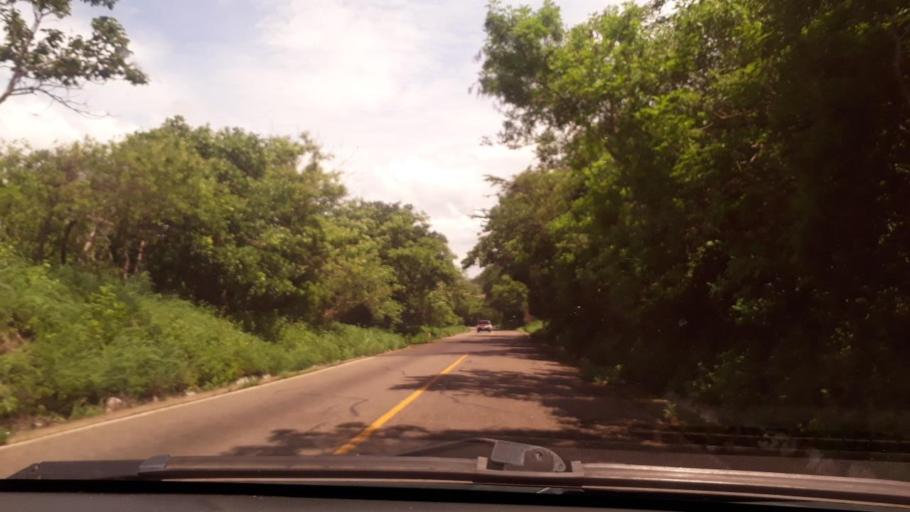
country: GT
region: Jutiapa
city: Jalpatagua
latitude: 14.1807
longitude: -90.0317
